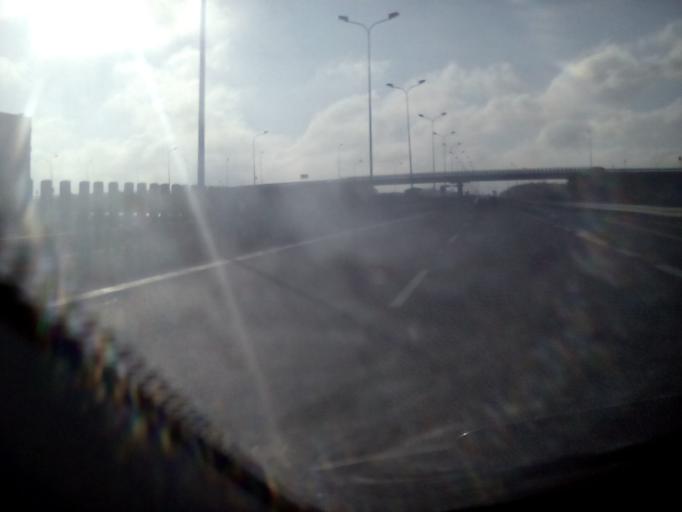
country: PL
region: Masovian Voivodeship
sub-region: Powiat grojecki
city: Goszczyn
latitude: 51.7617
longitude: 20.9035
